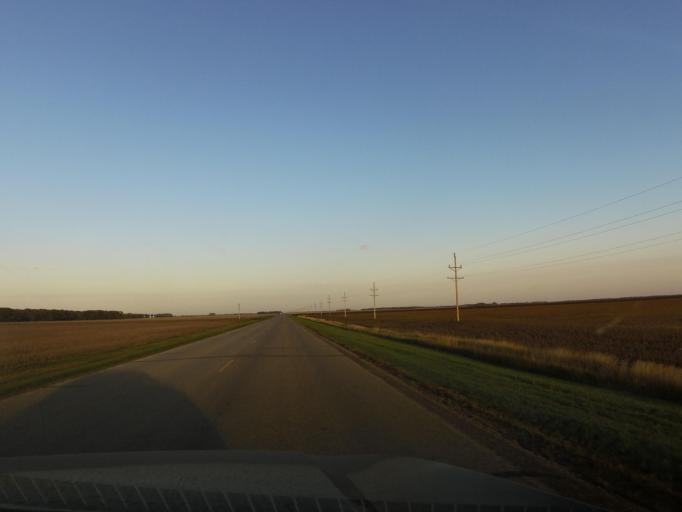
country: CA
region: Manitoba
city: Altona
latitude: 48.9634
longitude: -97.6404
